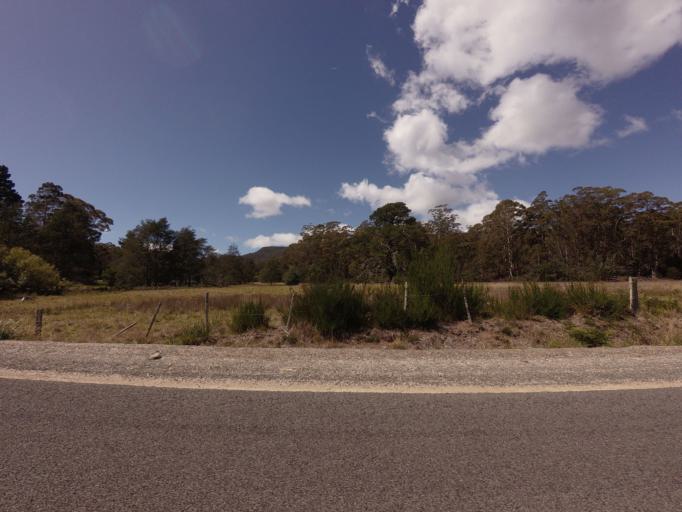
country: AU
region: Tasmania
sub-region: Break O'Day
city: St Helens
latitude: -41.6115
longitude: 148.2136
